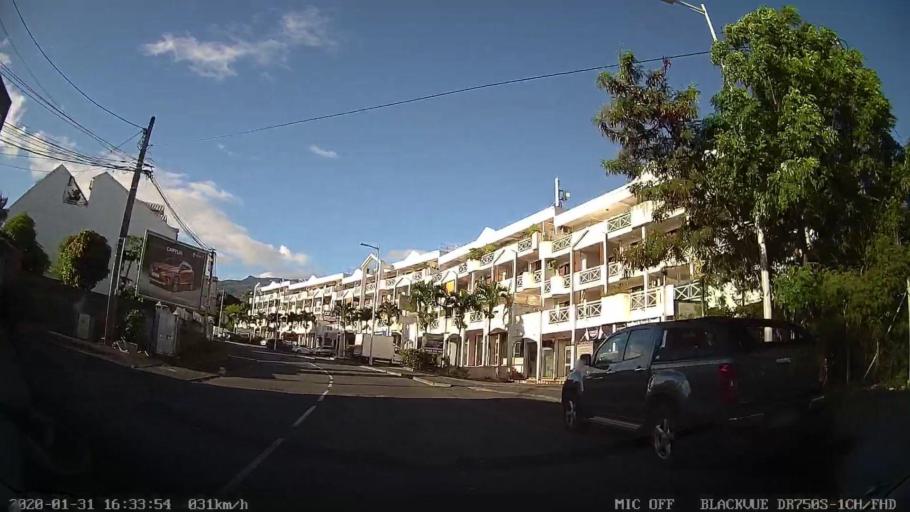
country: RE
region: Reunion
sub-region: Reunion
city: Saint-Denis
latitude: -20.8971
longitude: 55.4915
